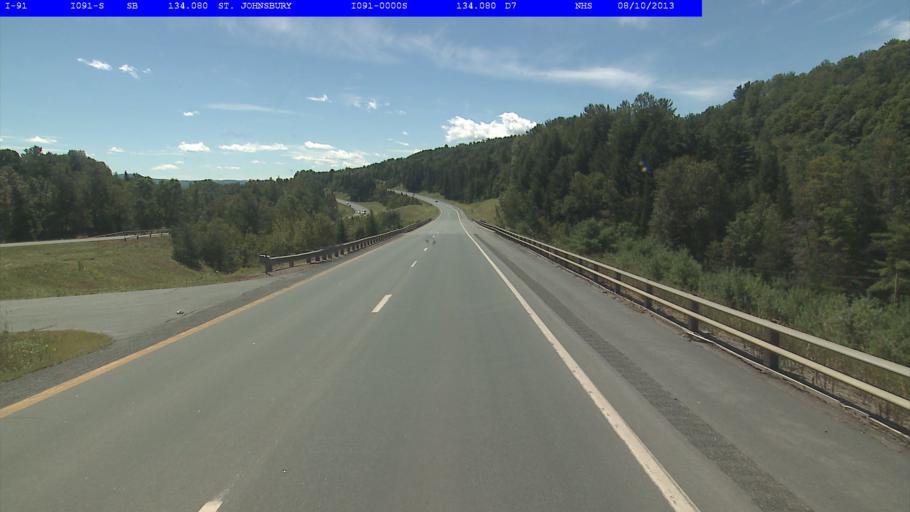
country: US
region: Vermont
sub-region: Caledonia County
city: Lyndon
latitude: 44.4761
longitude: -72.0245
